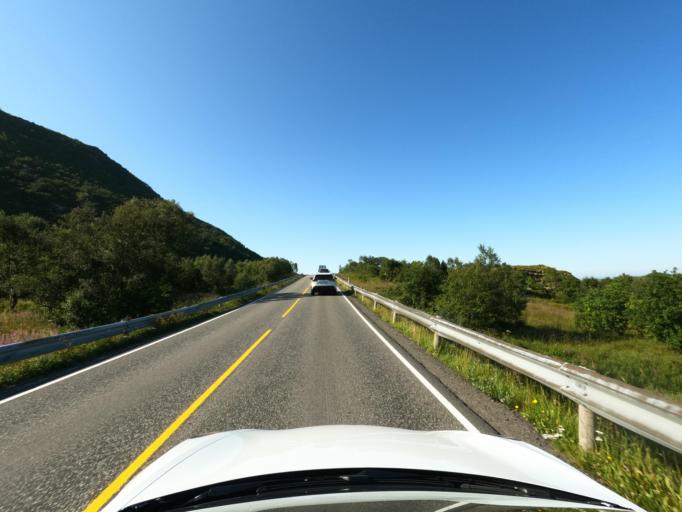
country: NO
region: Nordland
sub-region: Vagan
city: Kabelvag
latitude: 68.2755
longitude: 14.1375
